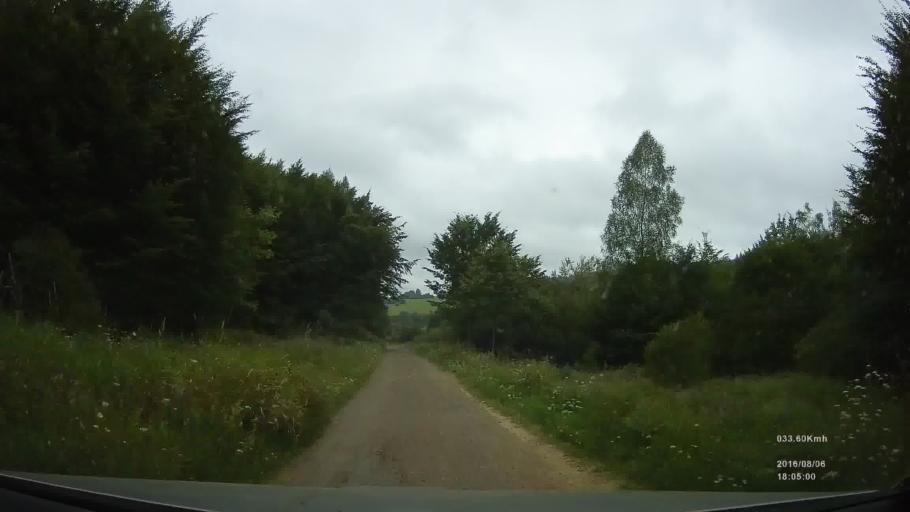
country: SK
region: Presovsky
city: Svidnik
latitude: 49.4098
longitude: 21.5680
